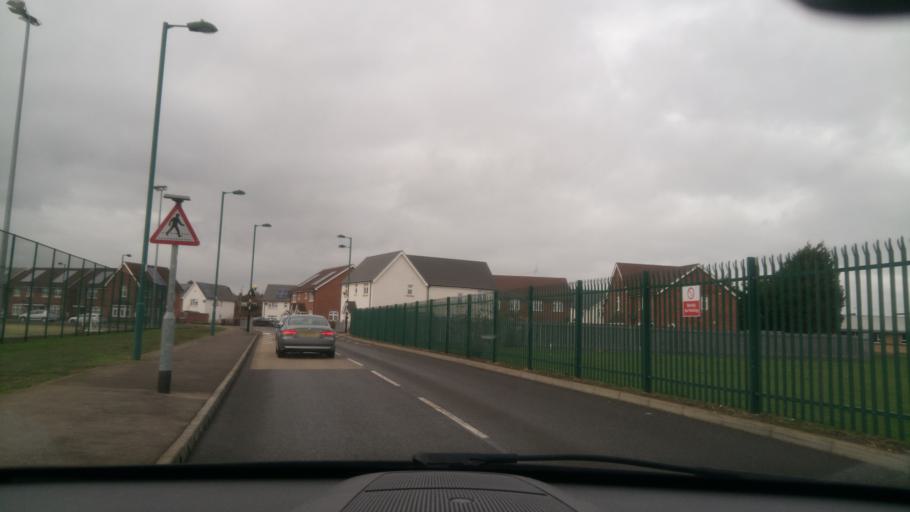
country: GB
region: England
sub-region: Peterborough
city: Peterborough
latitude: 52.5827
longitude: -0.2208
